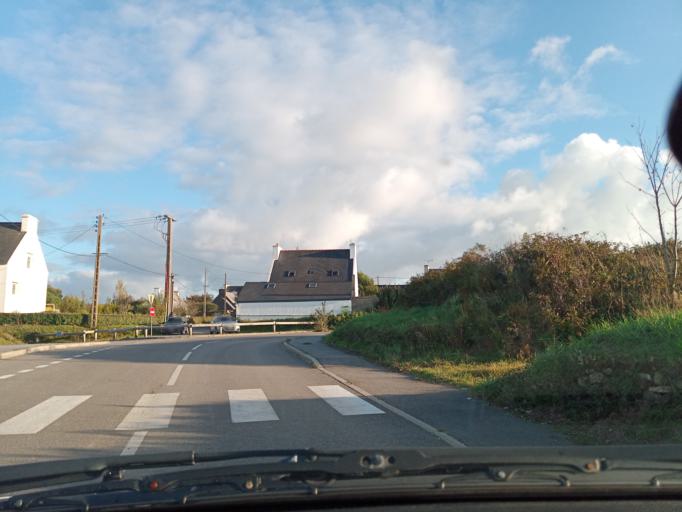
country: FR
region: Brittany
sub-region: Departement du Finistere
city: Esquibien
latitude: 48.0338
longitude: -4.5639
